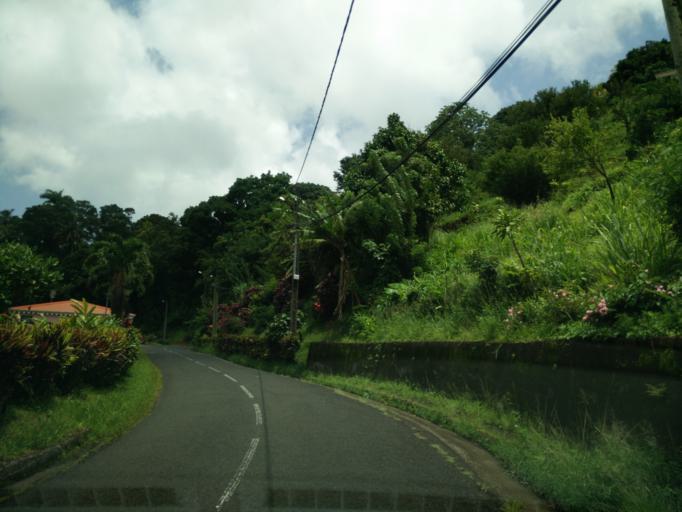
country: MQ
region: Martinique
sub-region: Martinique
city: Le Morne-Rouge
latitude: 14.7386
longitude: -61.1342
